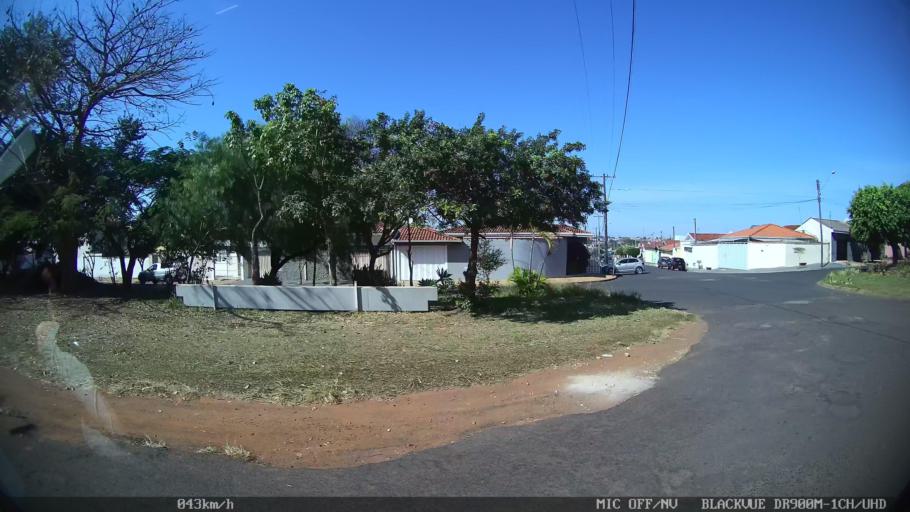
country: BR
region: Sao Paulo
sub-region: Batatais
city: Batatais
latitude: -20.8782
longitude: -47.5974
